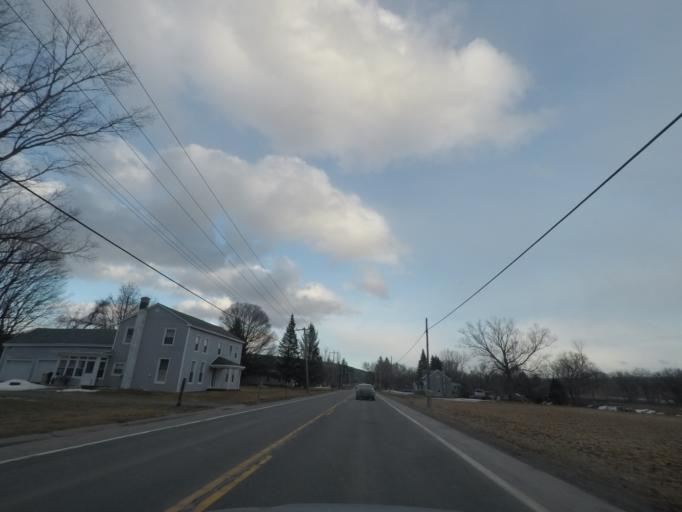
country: US
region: New York
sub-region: Herkimer County
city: Frankfort
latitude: 43.0563
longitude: -75.0786
